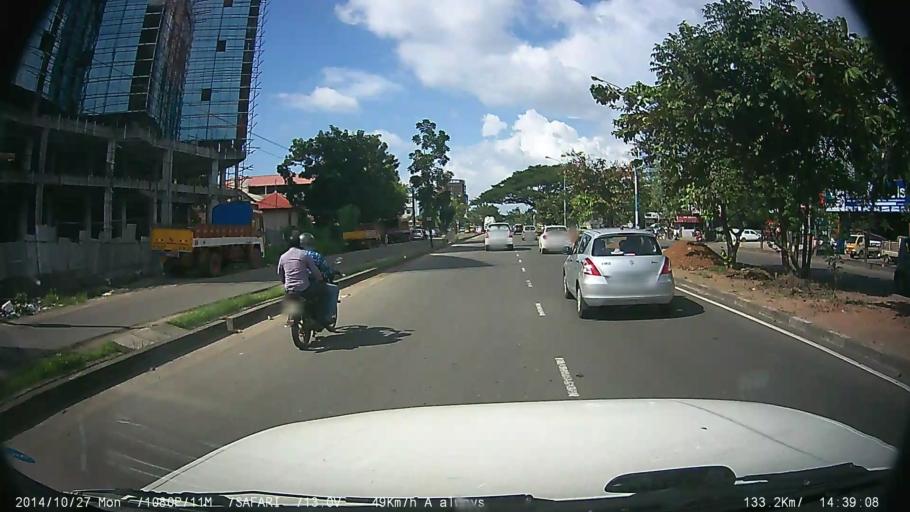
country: IN
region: Kerala
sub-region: Ernakulam
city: Cochin
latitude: 9.9880
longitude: 76.3158
